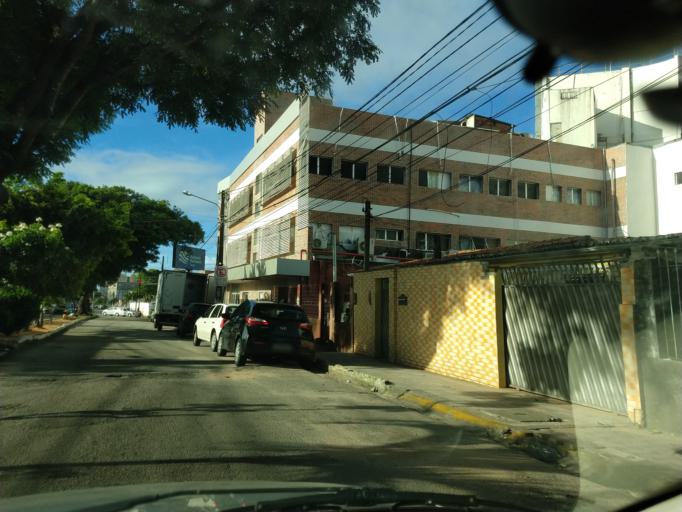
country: BR
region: Rio Grande do Norte
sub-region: Natal
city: Natal
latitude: -5.8040
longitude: -35.2129
